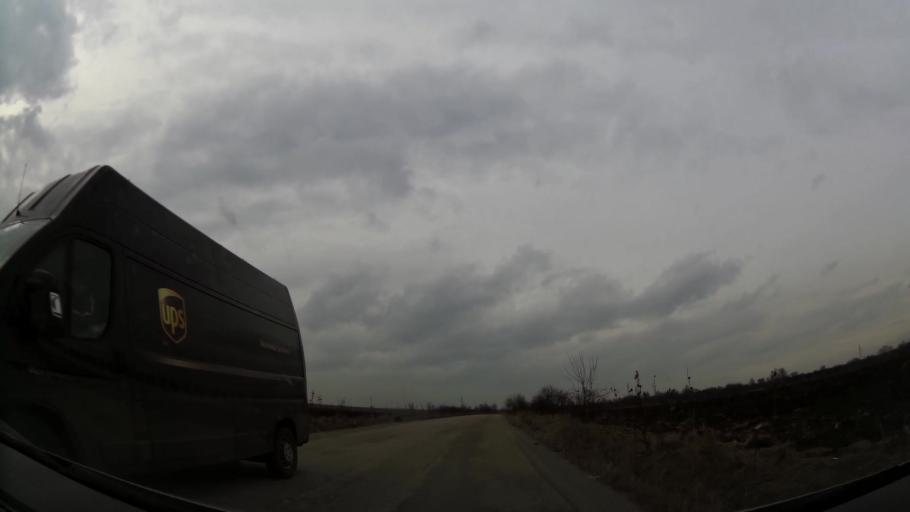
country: BG
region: Sofiya
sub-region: Obshtina Bozhurishte
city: Bozhurishte
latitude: 42.7049
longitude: 23.2180
